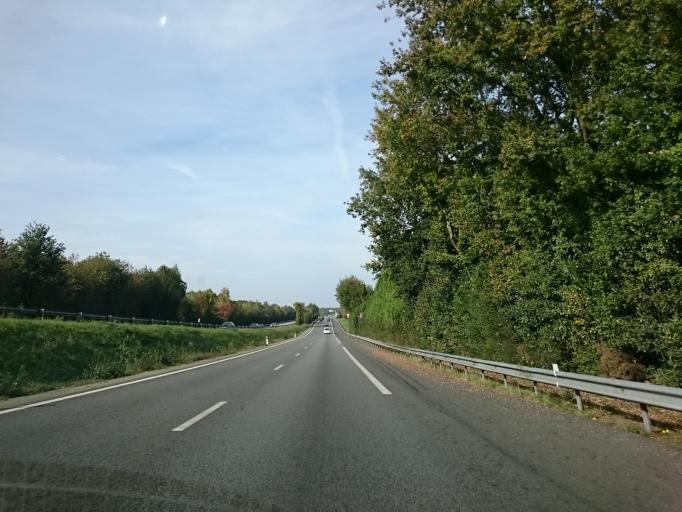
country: FR
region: Brittany
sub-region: Departement d'Ille-et-Vilaine
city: Crevin
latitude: 47.9561
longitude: -1.6823
